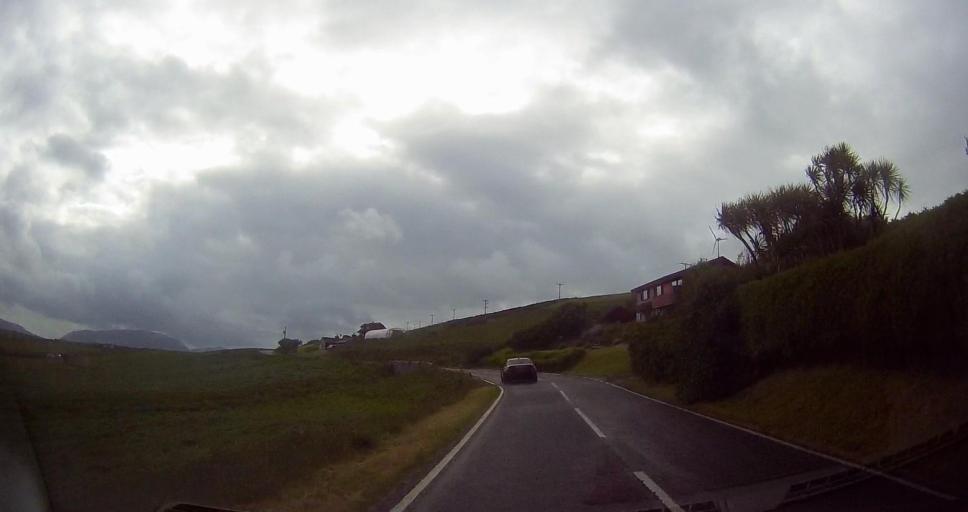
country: GB
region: Scotland
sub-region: Orkney Islands
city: Stromness
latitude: 58.9208
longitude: -3.1855
